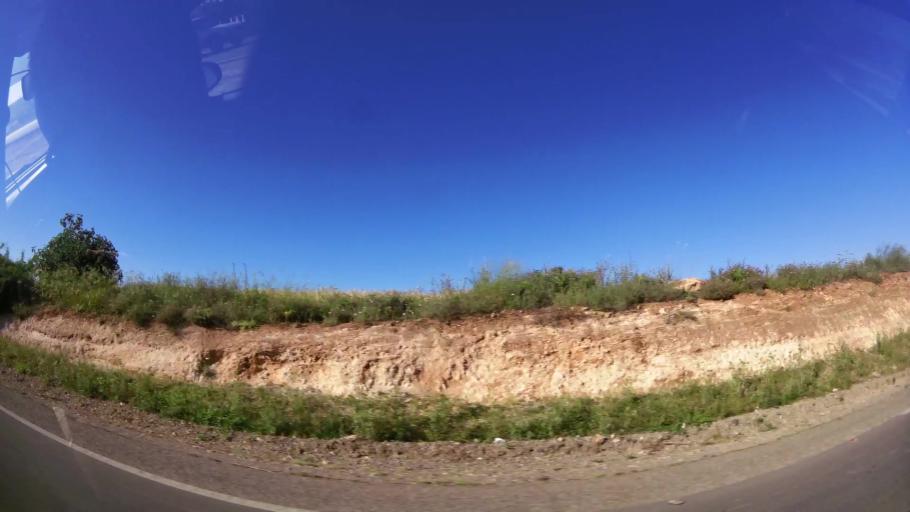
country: MA
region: Oriental
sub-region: Berkane-Taourirt
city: Ahfir
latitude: 34.9769
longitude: -2.1319
